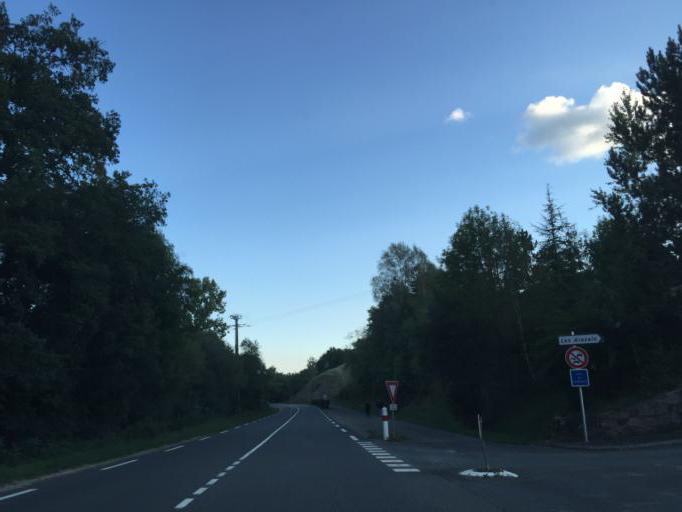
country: FR
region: Midi-Pyrenees
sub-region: Departement de l'Aveyron
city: Rodez
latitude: 44.3894
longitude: 2.5664
